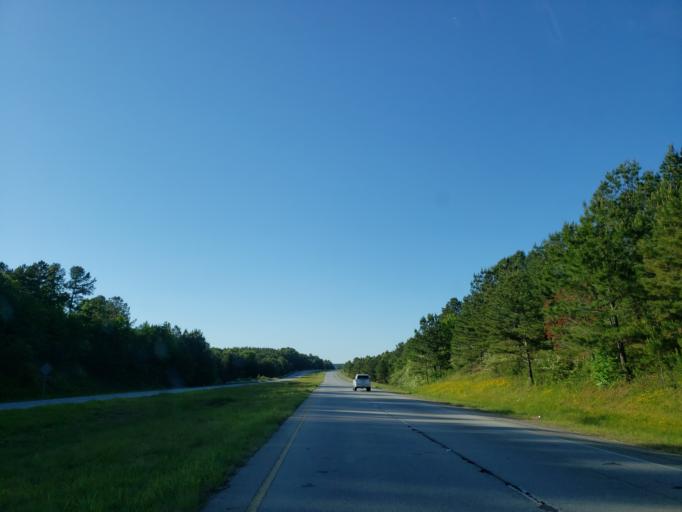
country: US
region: Georgia
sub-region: Polk County
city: Cedartown
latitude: 33.9226
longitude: -85.2459
